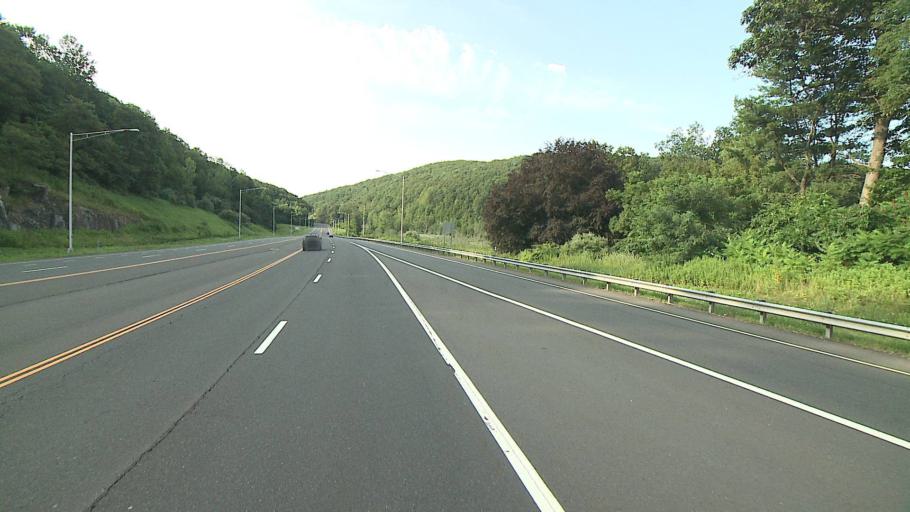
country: US
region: Connecticut
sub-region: Fairfield County
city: Danbury
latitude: 41.3675
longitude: -73.4744
